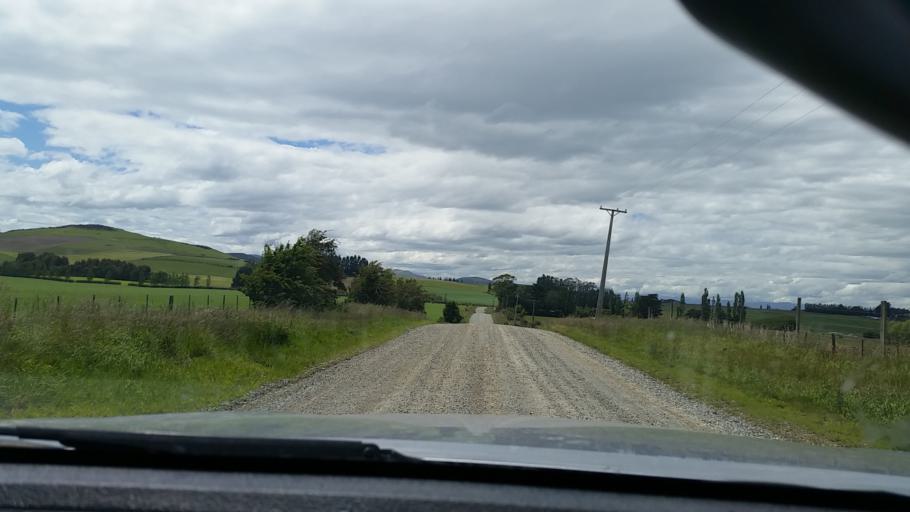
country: NZ
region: Southland
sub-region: Southland District
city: Winton
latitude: -45.7825
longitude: 168.5594
